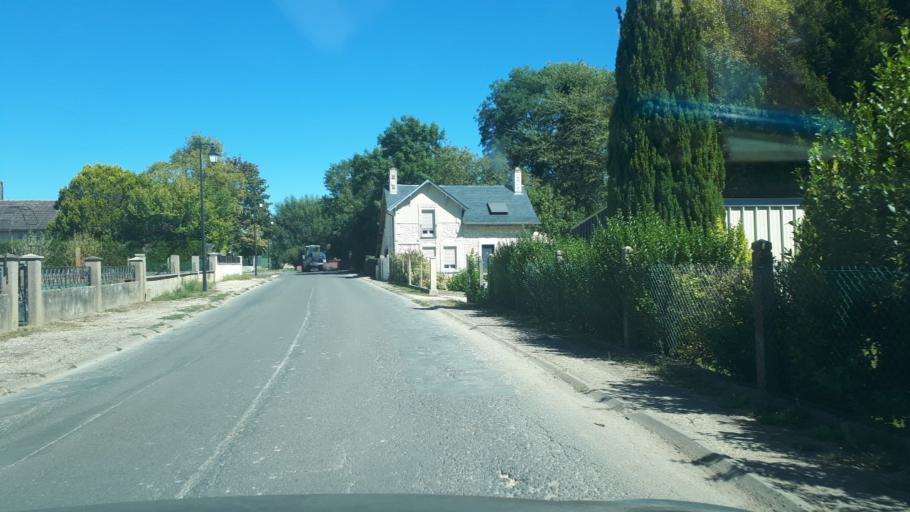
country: FR
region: Centre
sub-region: Departement du Cher
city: Sainte-Solange
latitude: 47.1385
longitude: 2.5529
